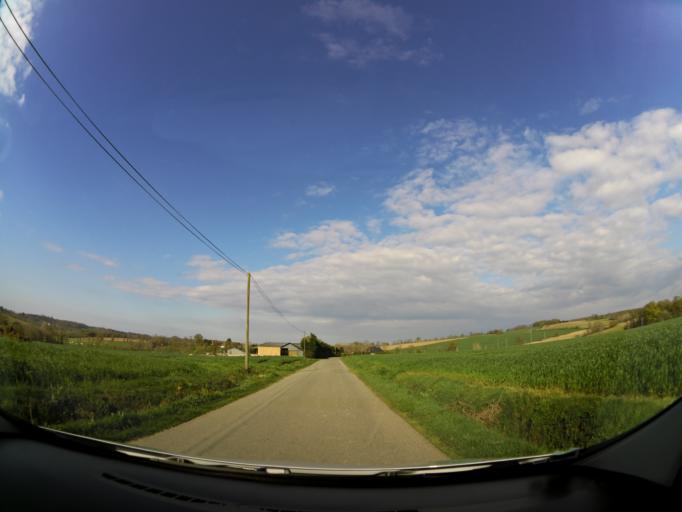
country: FR
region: Brittany
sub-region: Departement d'Ille-et-Vilaine
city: Crevin
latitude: 47.9409
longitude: -1.6928
